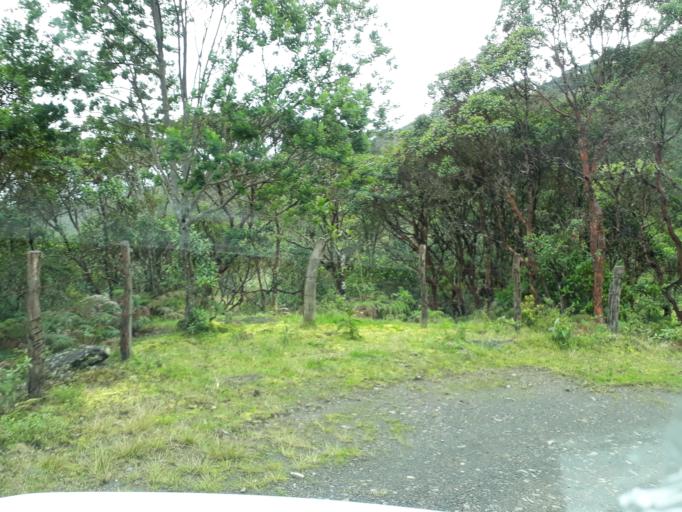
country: CO
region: Cundinamarca
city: Junin
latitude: 4.7301
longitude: -73.6266
